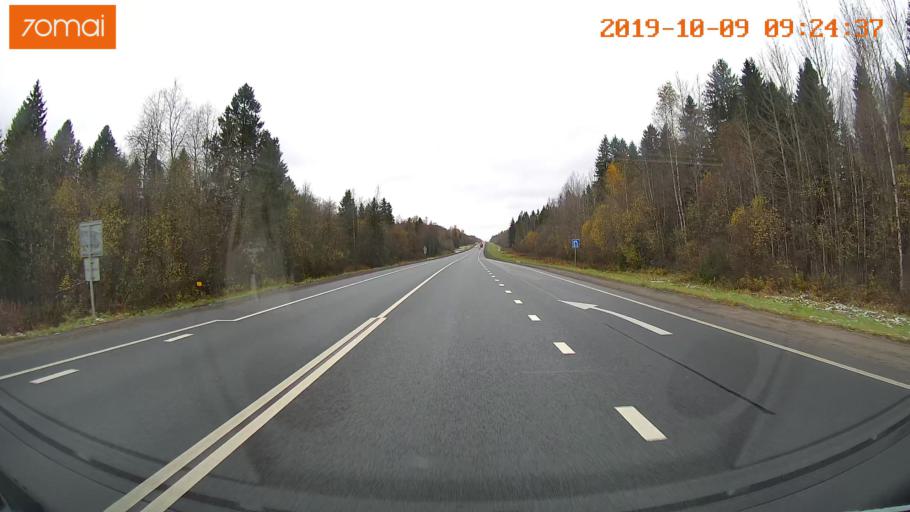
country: RU
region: Vologda
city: Vologda
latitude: 59.0810
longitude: 40.0135
